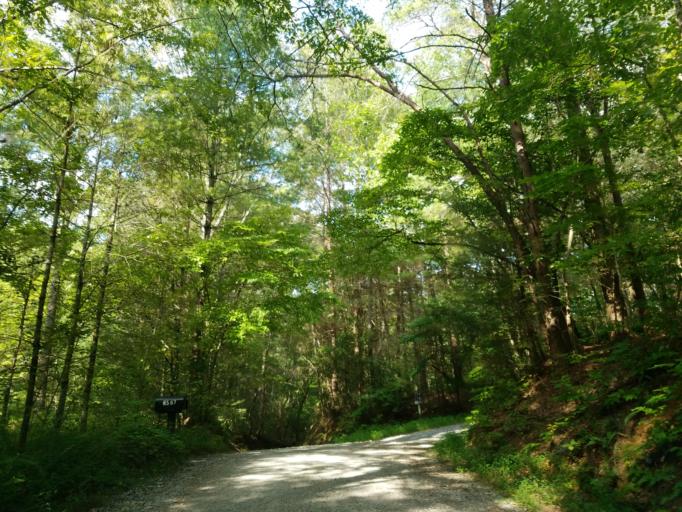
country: US
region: Georgia
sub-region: Gilmer County
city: Ellijay
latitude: 34.7862
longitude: -84.4195
